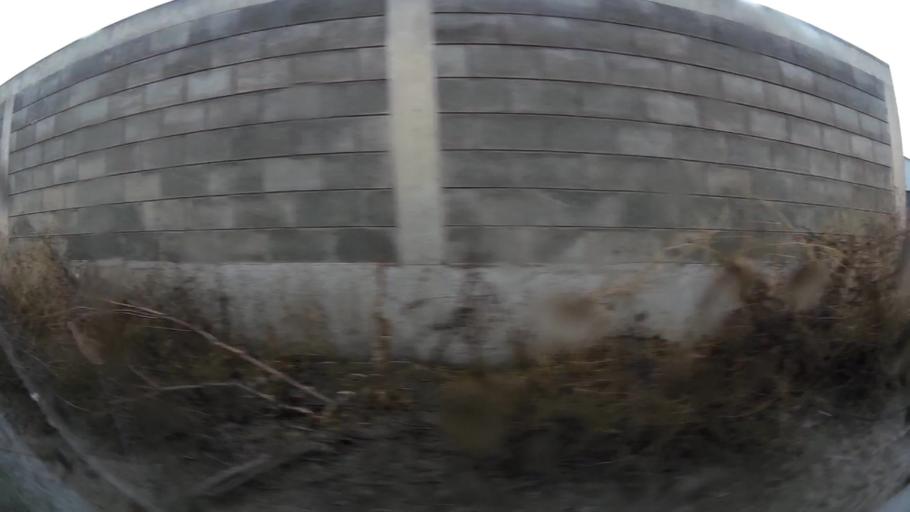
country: BG
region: Sofia-Capital
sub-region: Stolichna Obshtina
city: Sofia
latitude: 42.6645
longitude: 23.4197
